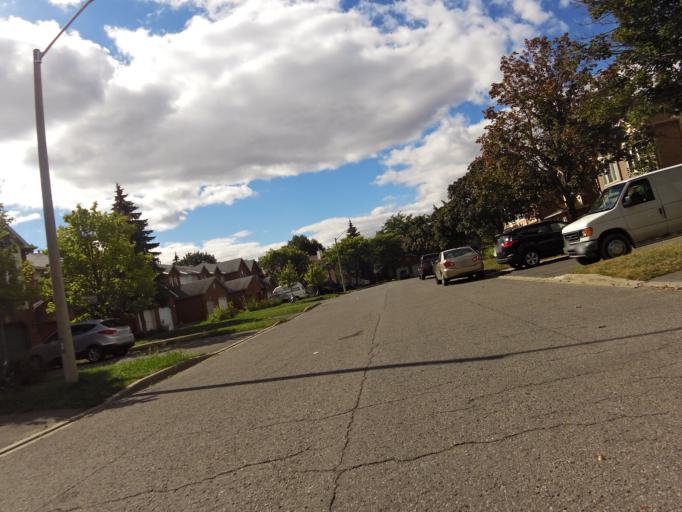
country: CA
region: Ontario
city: Ottawa
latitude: 45.3587
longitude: -75.6359
